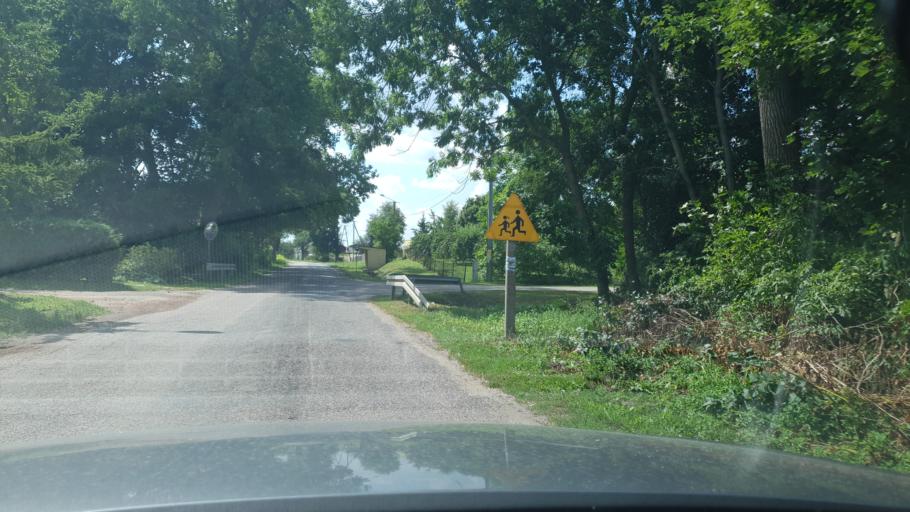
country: PL
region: Kujawsko-Pomorskie
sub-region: Powiat wabrzeski
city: Pluznica
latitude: 53.2649
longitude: 18.8361
